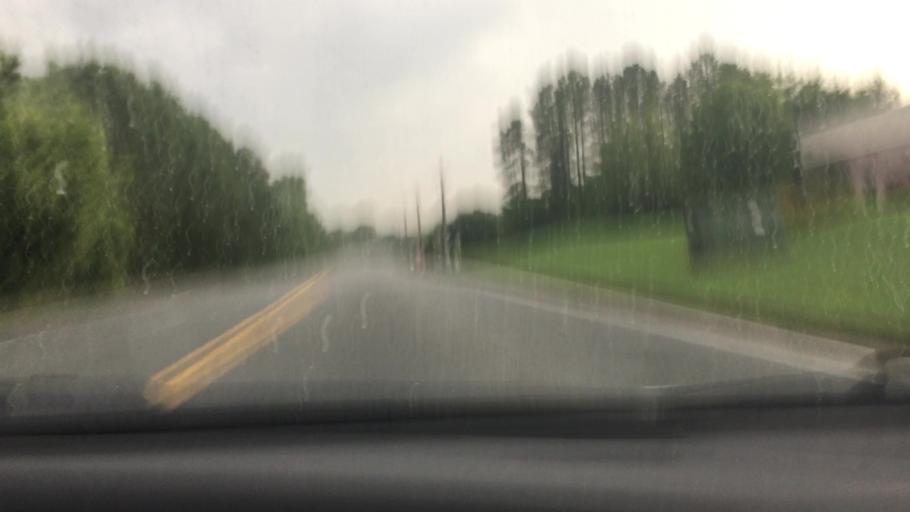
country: US
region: Georgia
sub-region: Fulton County
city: Union City
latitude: 33.6450
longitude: -84.5216
